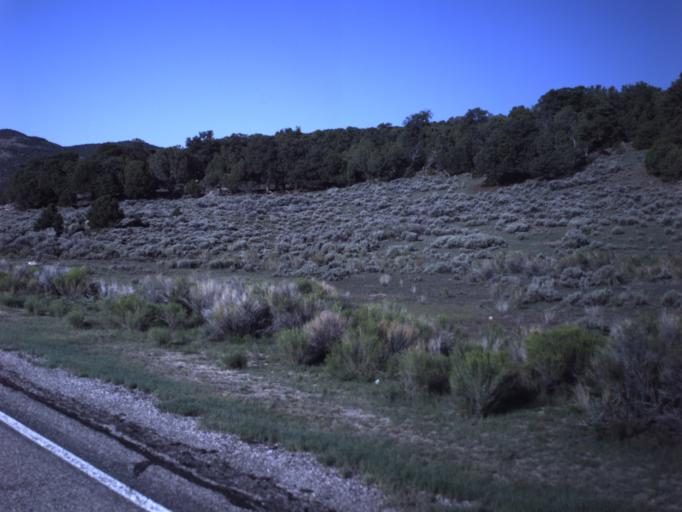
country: US
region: Utah
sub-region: Wayne County
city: Loa
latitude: 38.6831
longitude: -111.3977
